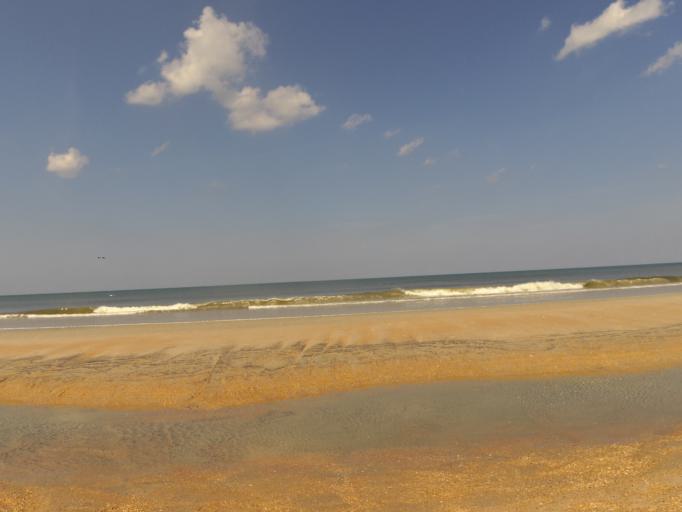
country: US
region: Florida
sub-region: Saint Johns County
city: Palm Valley
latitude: 30.1550
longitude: -81.3538
